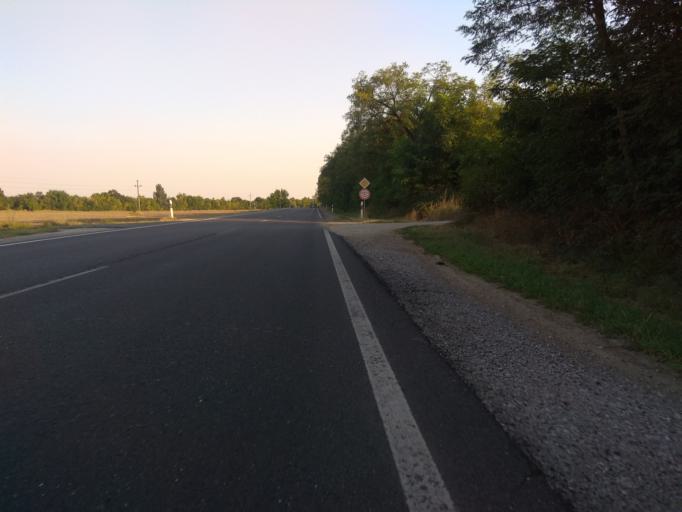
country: HU
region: Borsod-Abauj-Zemplen
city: Nyekladhaza
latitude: 47.9660
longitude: 20.8328
